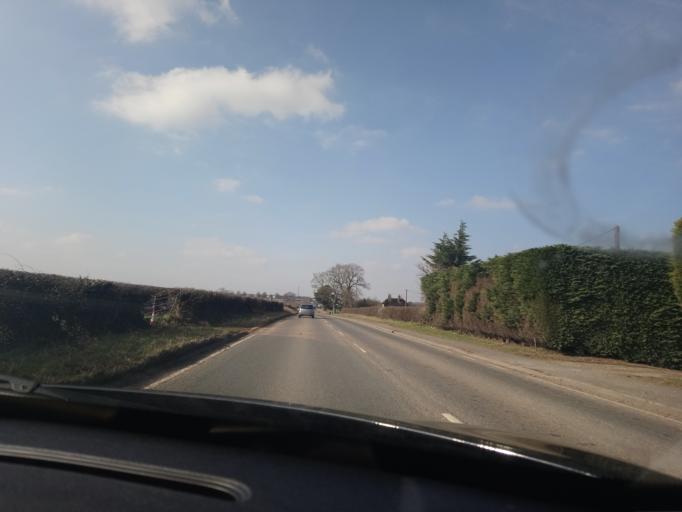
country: GB
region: England
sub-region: Shropshire
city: Berrington
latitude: 52.6881
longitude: -2.7007
